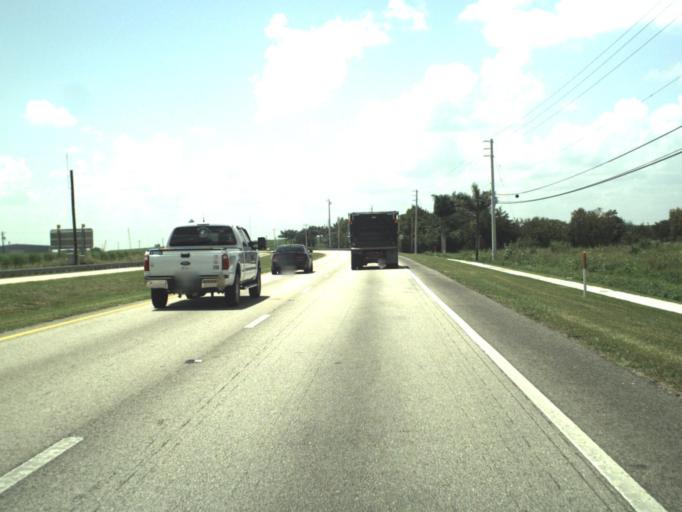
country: US
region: Florida
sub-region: Palm Beach County
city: South Bay
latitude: 26.6785
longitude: -80.7269
